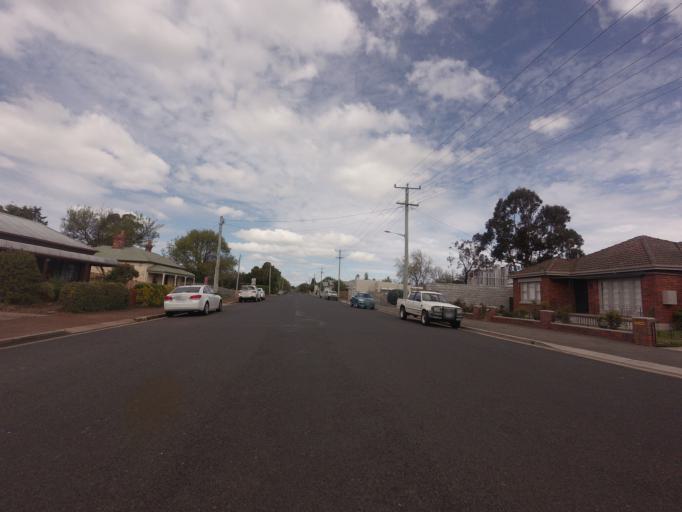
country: AU
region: Tasmania
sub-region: Northern Midlands
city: Longford
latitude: -41.5959
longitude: 147.1227
